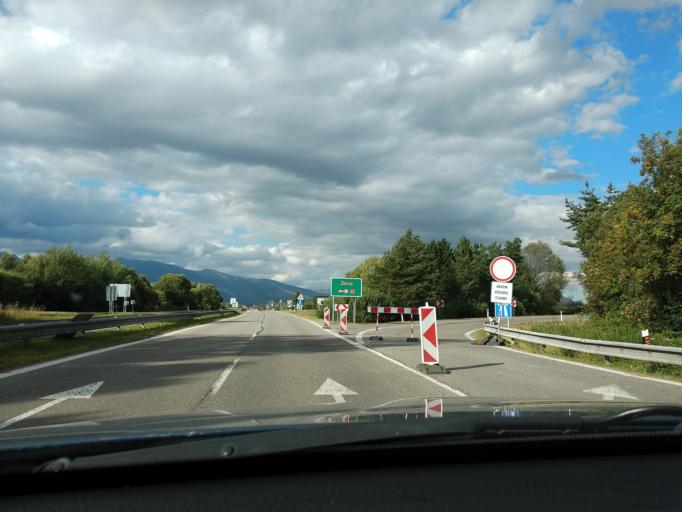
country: SK
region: Zilinsky
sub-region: Okres Zilina
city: Liptovsky Hradok
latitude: 49.0603
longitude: 19.7481
